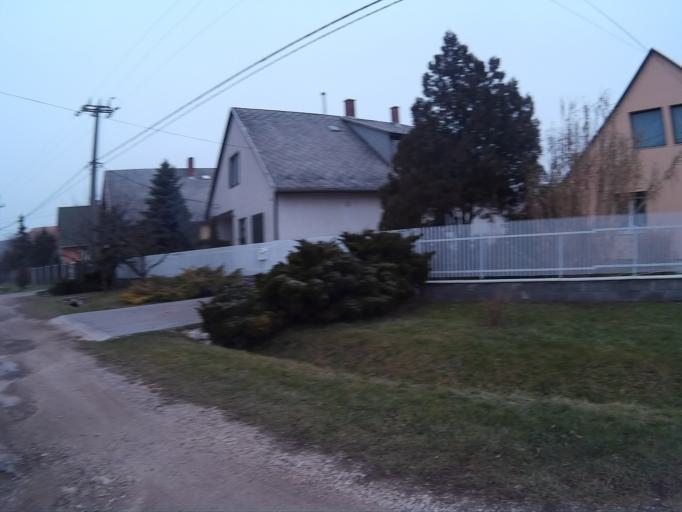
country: HU
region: Fejer
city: Csakvar
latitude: 47.3872
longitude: 18.4582
